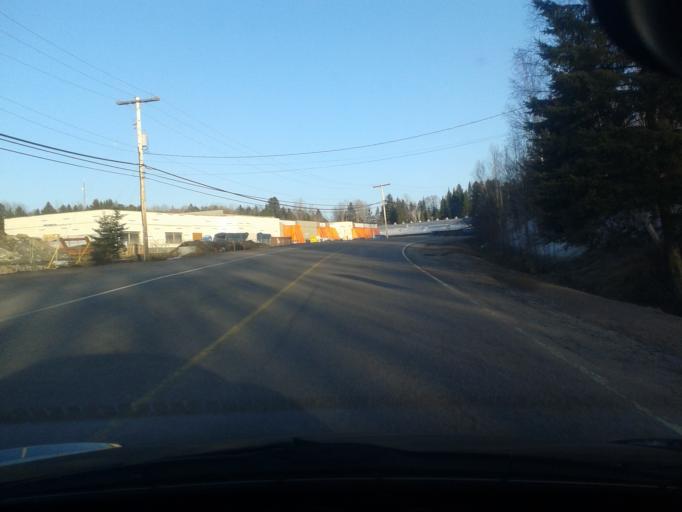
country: CA
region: Ontario
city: Powassan
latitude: 46.1873
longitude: -79.2887
